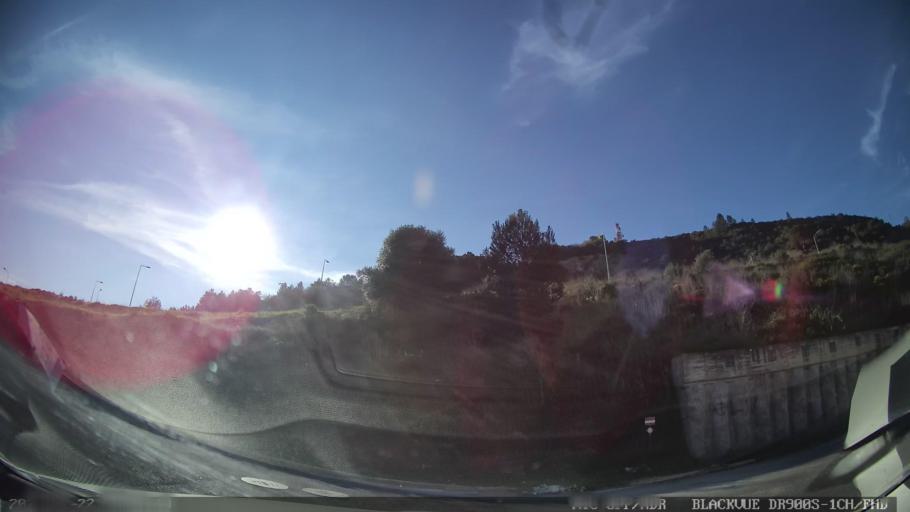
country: PT
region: Lisbon
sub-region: Vila Franca de Xira
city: Vila Franca de Xira
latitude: 38.9613
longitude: -8.9895
